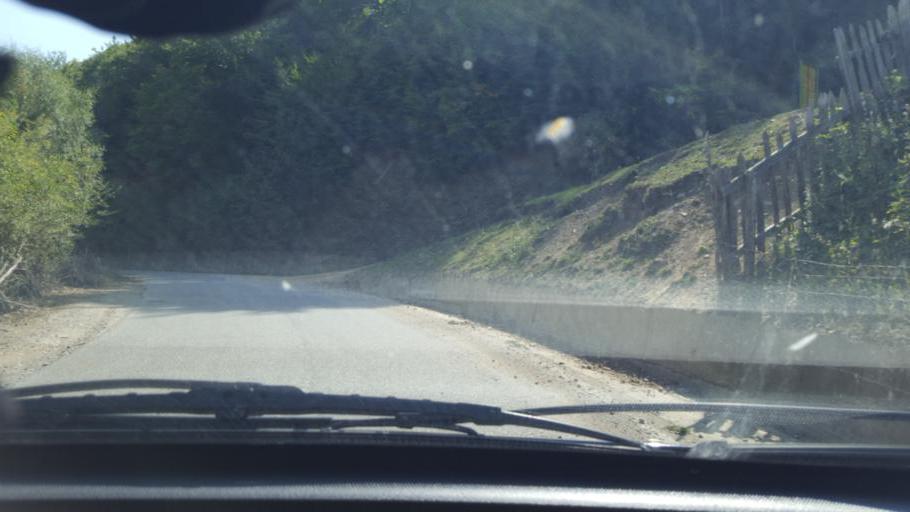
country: ME
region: Andrijevica
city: Andrijevica
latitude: 42.5813
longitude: 19.7348
